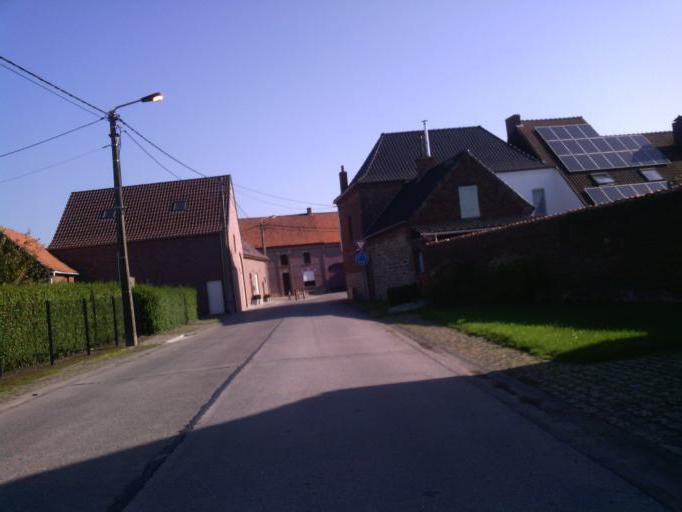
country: BE
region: Wallonia
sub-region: Province du Hainaut
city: Peruwelz
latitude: 50.5657
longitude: 3.6428
